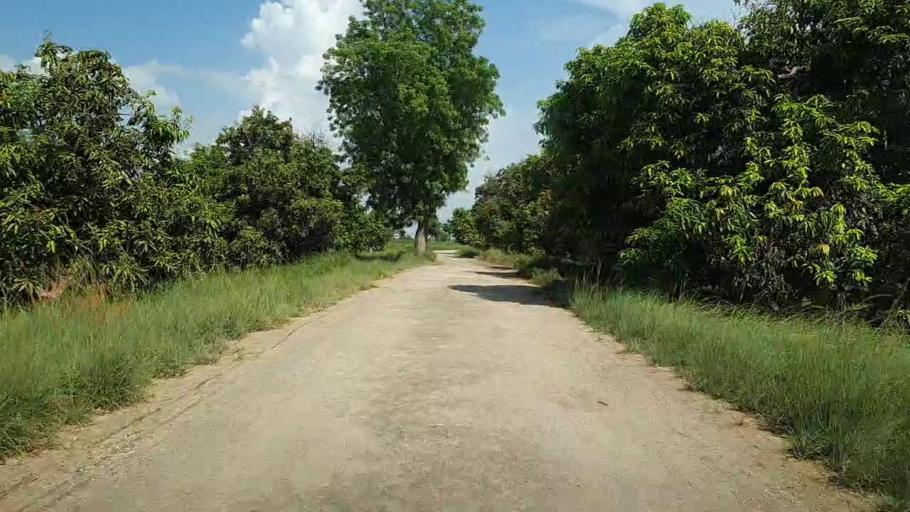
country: PK
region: Sindh
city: Bhiria
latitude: 26.9091
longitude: 68.2248
